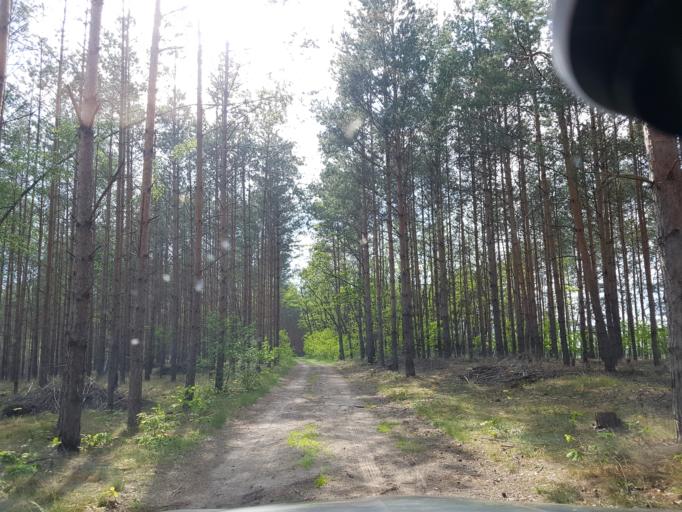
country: DE
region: Brandenburg
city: Schonewalde
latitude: 51.6367
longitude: 13.6274
